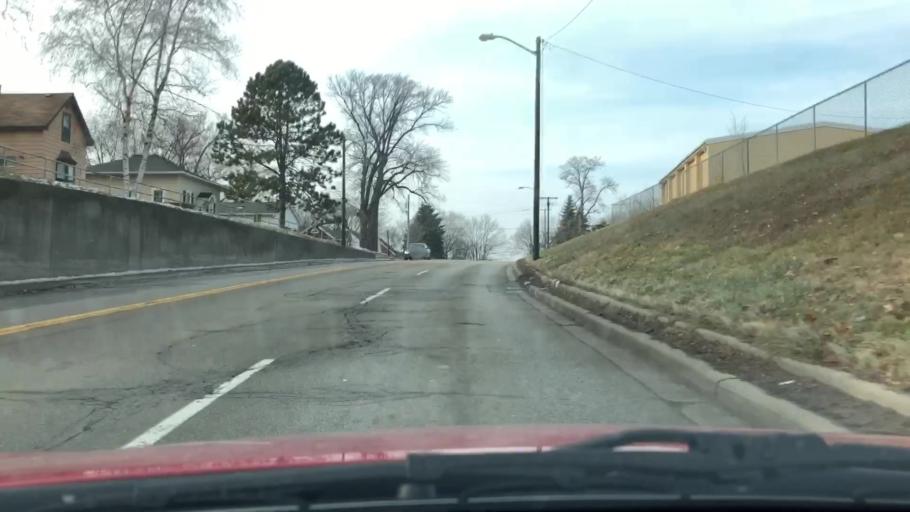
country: US
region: Wisconsin
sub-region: Brown County
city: De Pere
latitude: 44.4483
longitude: -88.0773
